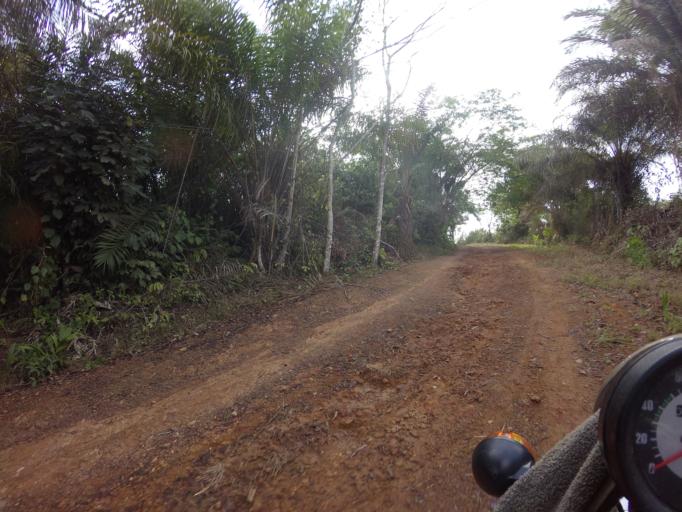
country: SL
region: Southern Province
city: Zimmi
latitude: 7.1488
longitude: -11.2037
